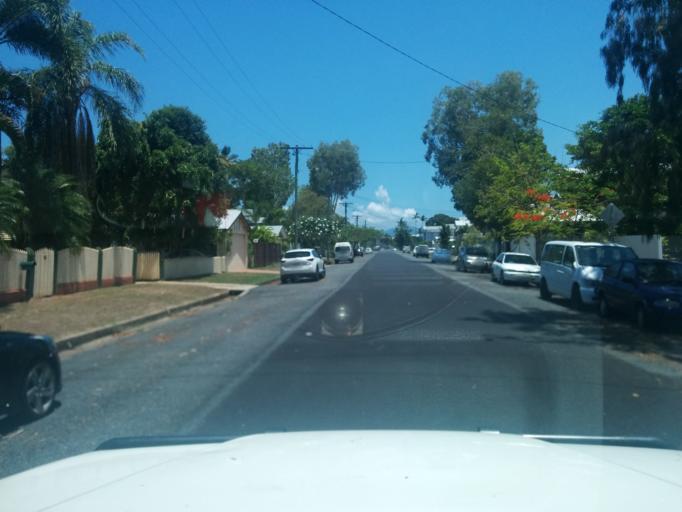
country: AU
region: Queensland
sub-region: Cairns
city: Cairns
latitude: -16.9063
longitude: 145.7569
